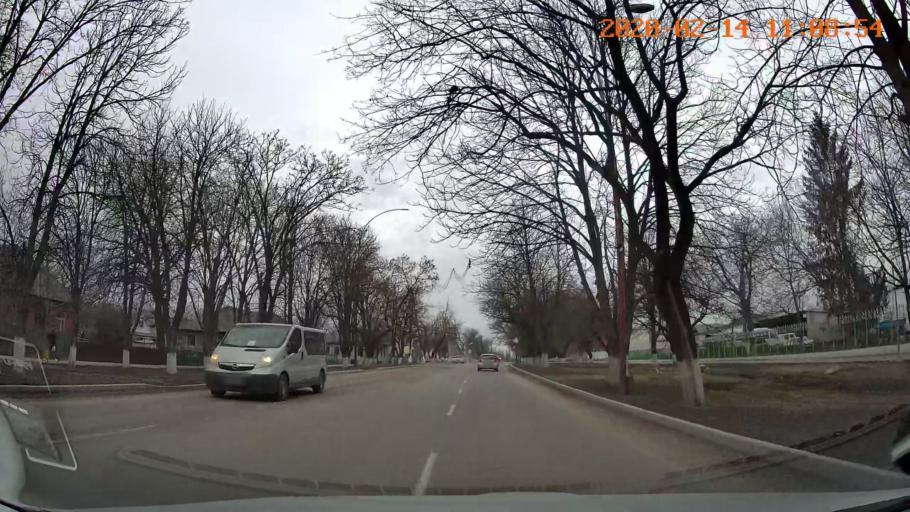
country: MD
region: Raionul Edinet
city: Edinet
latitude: 48.1749
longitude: 27.2979
